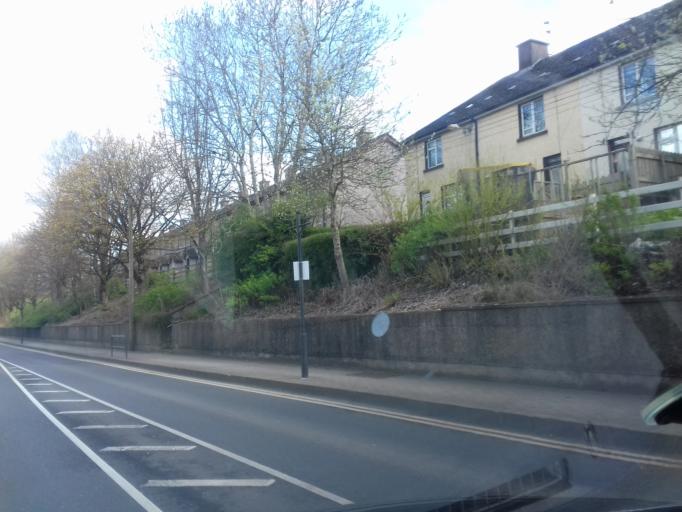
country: IE
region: Ulster
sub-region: An Cabhan
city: Cavan
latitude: 53.9849
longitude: -7.3592
